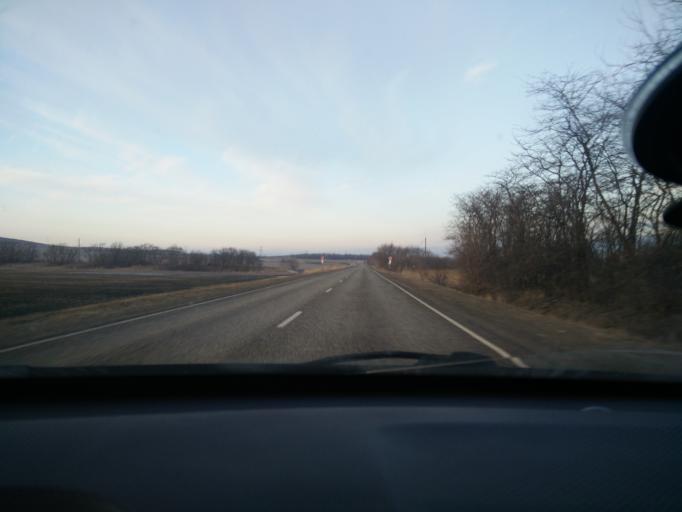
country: RU
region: Stavropol'skiy
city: Balakhonovskoye
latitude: 44.9948
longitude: 41.7268
